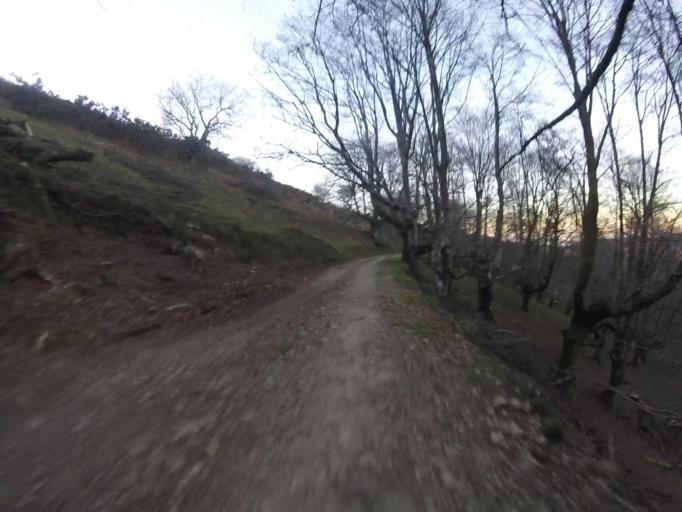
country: ES
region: Navarre
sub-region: Provincia de Navarra
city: Arano
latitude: 43.2540
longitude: -1.8252
